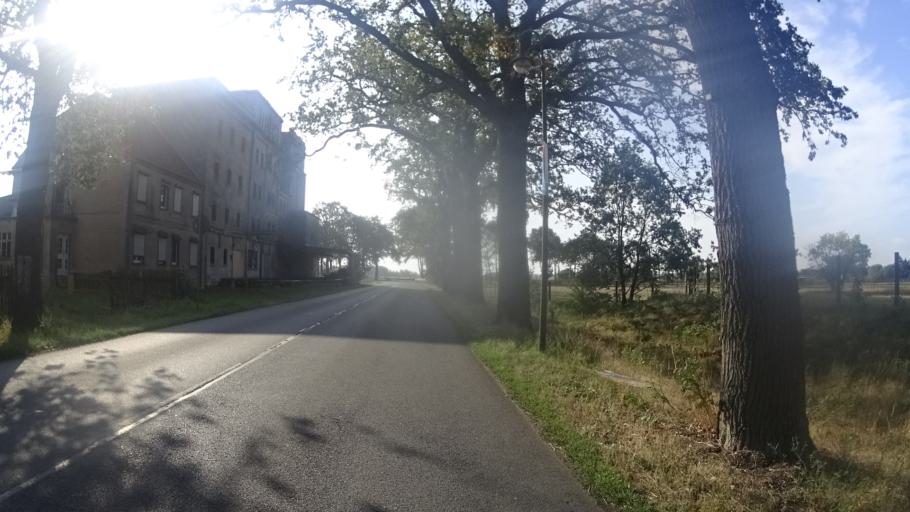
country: DE
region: Brandenburg
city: Cumlosen
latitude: 53.0293
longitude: 11.6591
